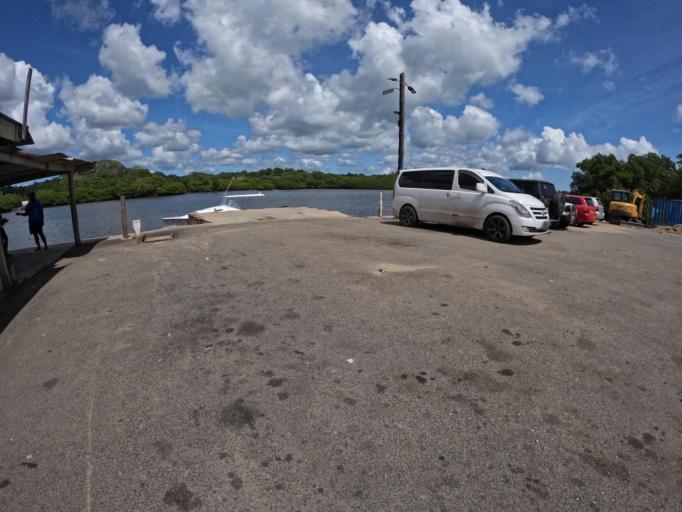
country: FJ
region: Central
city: Suva
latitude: -17.9787
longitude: 178.6009
